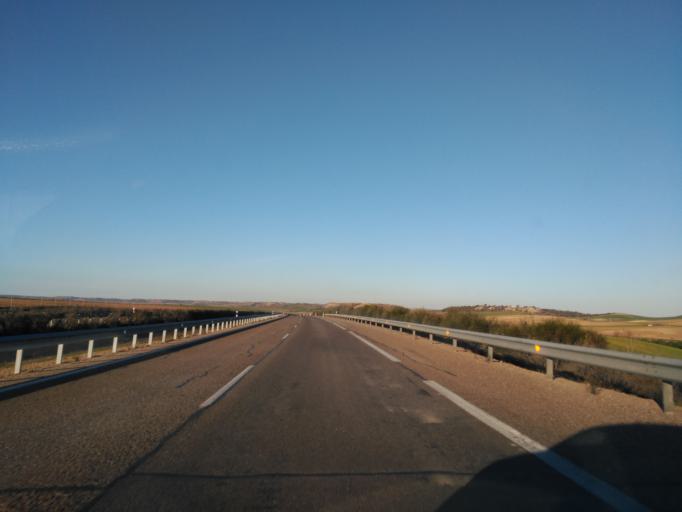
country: ES
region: Castille and Leon
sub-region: Provincia de Zamora
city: Canizal
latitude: 41.1844
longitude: -5.3609
